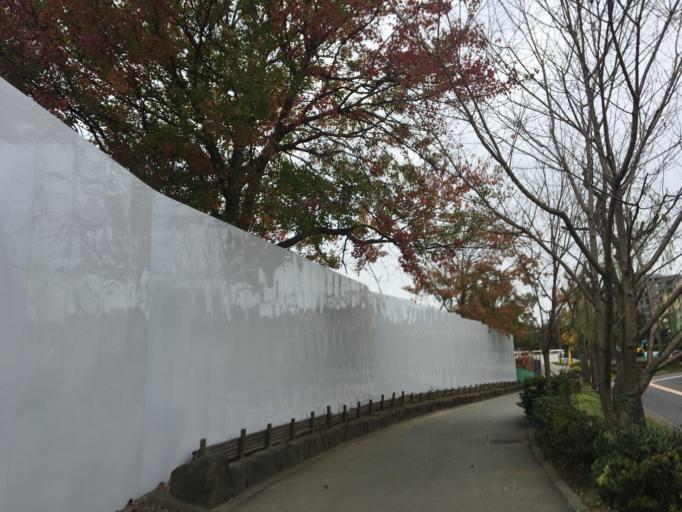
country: JP
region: Tokyo
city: Urayasu
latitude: 35.6496
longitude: 139.8823
